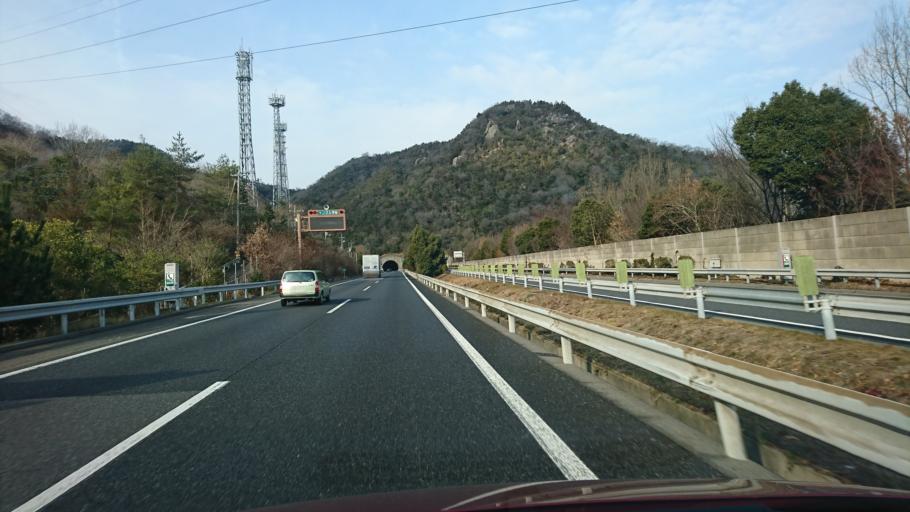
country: JP
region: Hyogo
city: Kariya
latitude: 34.7874
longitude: 134.1527
